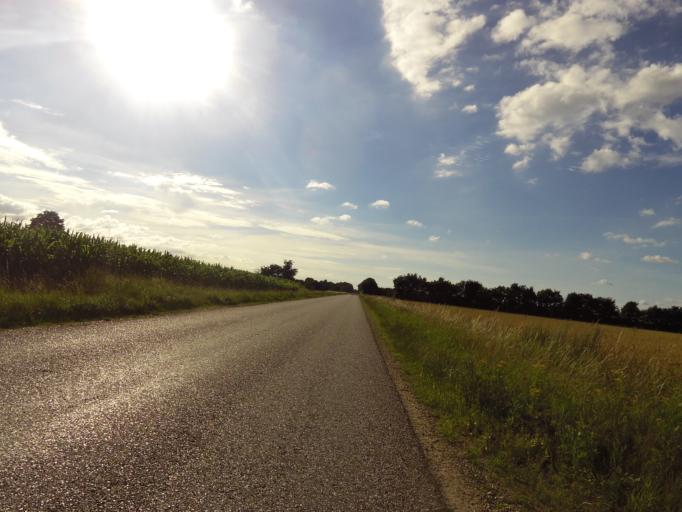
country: DK
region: South Denmark
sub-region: Haderslev Kommune
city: Vojens
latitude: 55.2026
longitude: 9.2854
